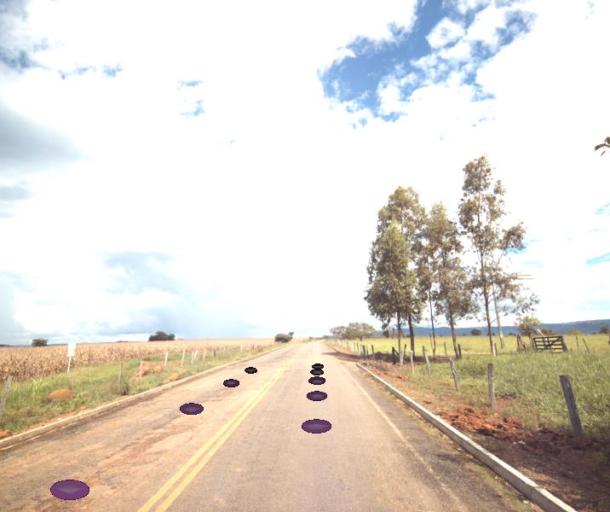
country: BR
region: Goias
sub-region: Pirenopolis
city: Pirenopolis
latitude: -16.0257
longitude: -49.1095
